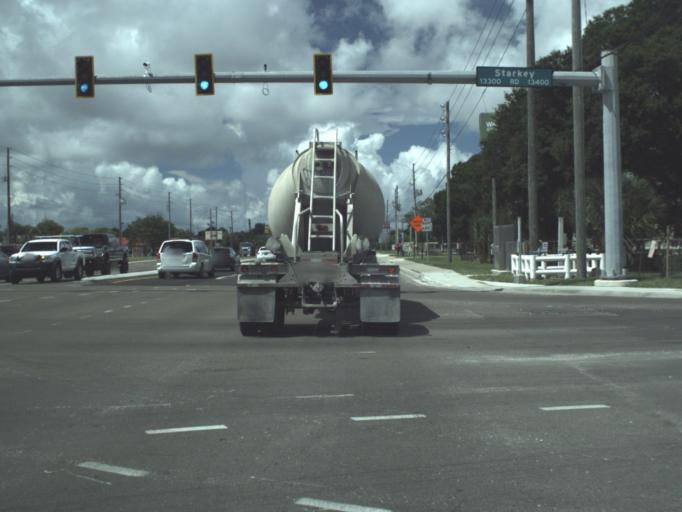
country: US
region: Florida
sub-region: Pinellas County
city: Largo
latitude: 27.8946
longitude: -82.7623
